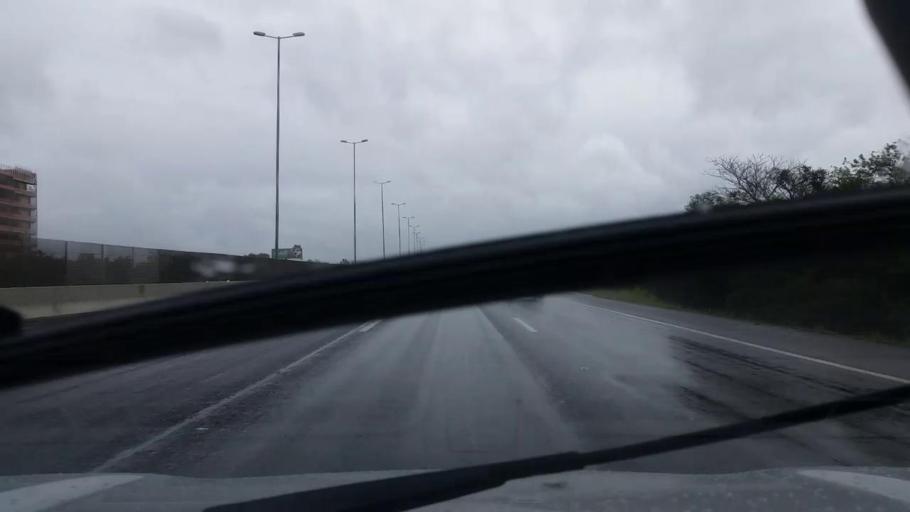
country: BR
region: Rio Grande do Sul
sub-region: Canoas
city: Canoas
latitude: -29.9681
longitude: -51.1583
